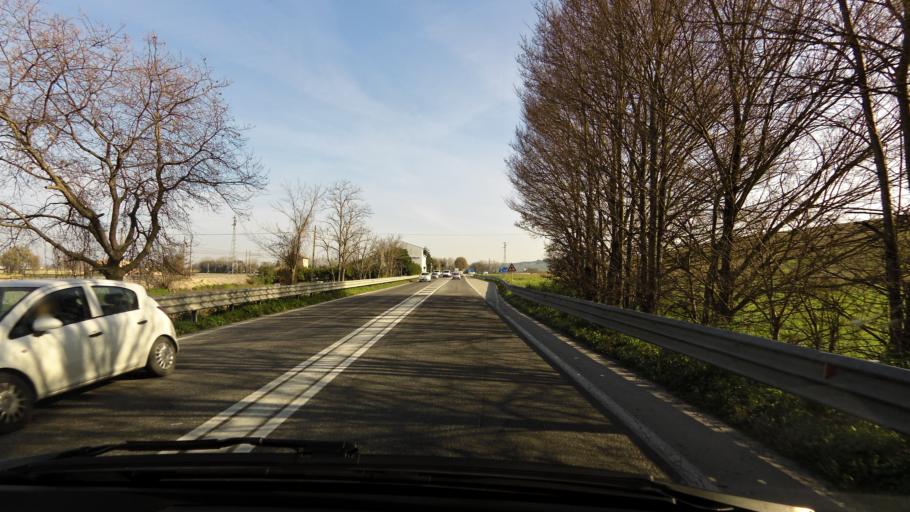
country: IT
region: The Marches
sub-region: Provincia di Ancona
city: Villa Musone
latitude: 43.4675
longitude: 13.6010
